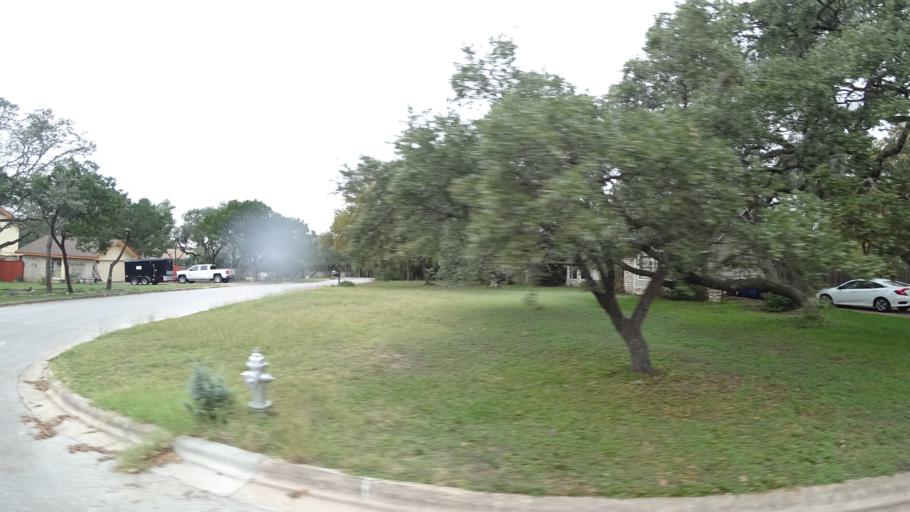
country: US
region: Texas
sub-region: Williamson County
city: Anderson Mill
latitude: 30.4445
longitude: -97.8149
